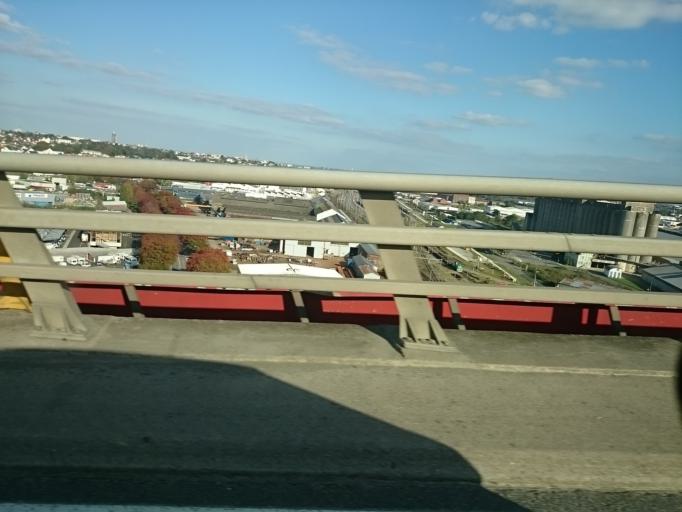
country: FR
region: Pays de la Loire
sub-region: Departement de la Loire-Atlantique
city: Bouguenais
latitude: 47.1953
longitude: -1.6137
